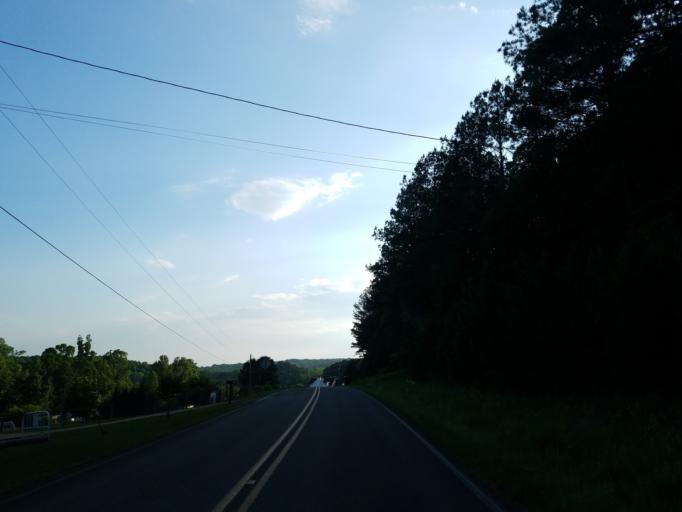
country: US
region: Georgia
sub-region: Cherokee County
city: Ball Ground
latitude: 34.3001
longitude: -84.3705
